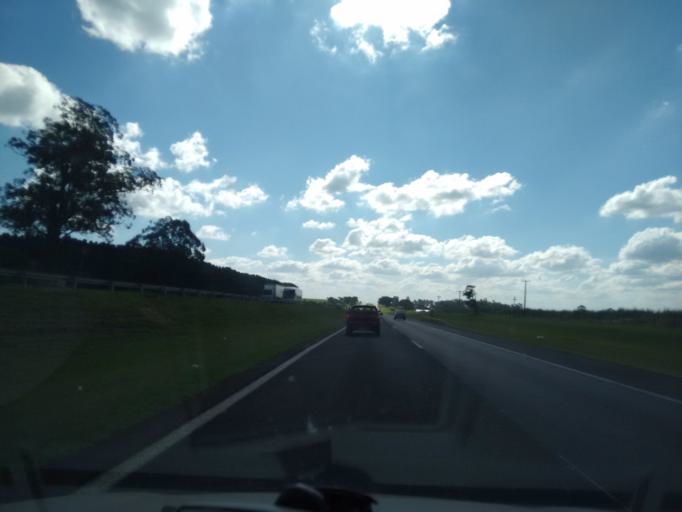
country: BR
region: Sao Paulo
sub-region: Ibate
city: Ibate
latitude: -21.9281
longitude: -48.0239
